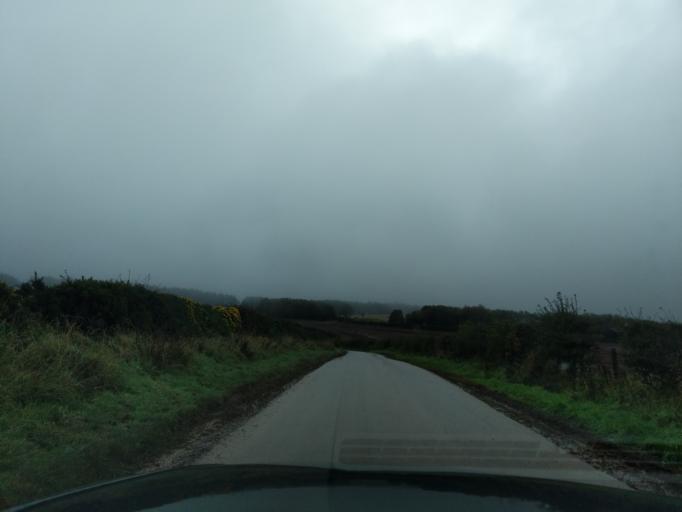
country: GB
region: Scotland
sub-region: East Lothian
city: Dunbar
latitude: 55.9356
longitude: -2.4099
